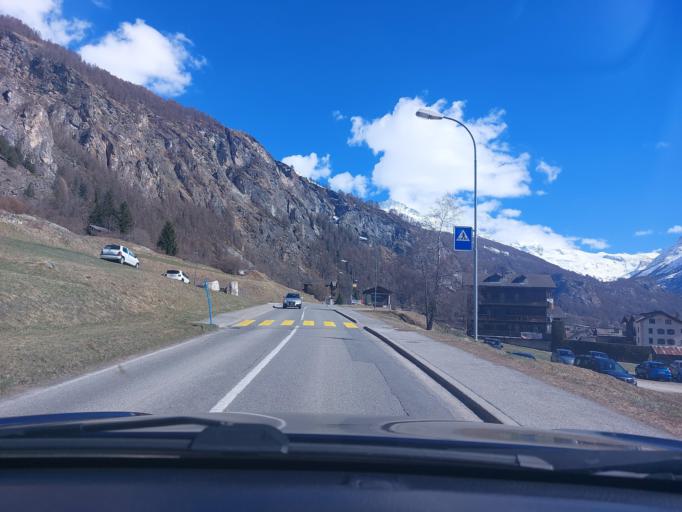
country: CH
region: Valais
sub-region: Herens District
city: Evolene
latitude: 46.1160
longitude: 7.4906
